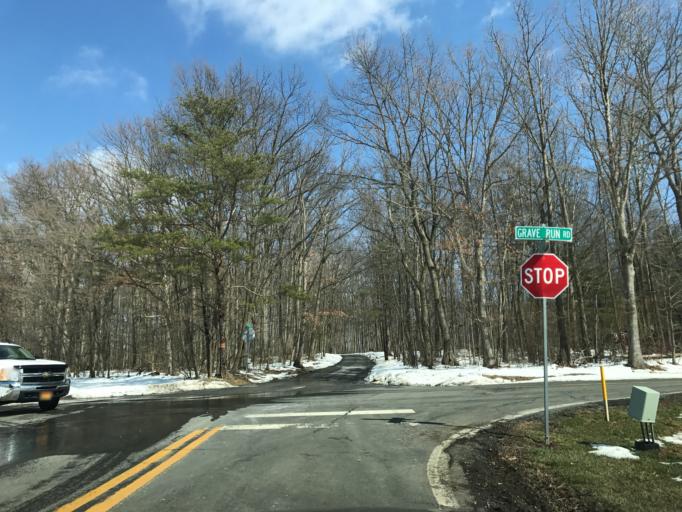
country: US
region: Maryland
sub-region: Carroll County
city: Manchester
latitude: 39.7207
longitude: -76.8082
